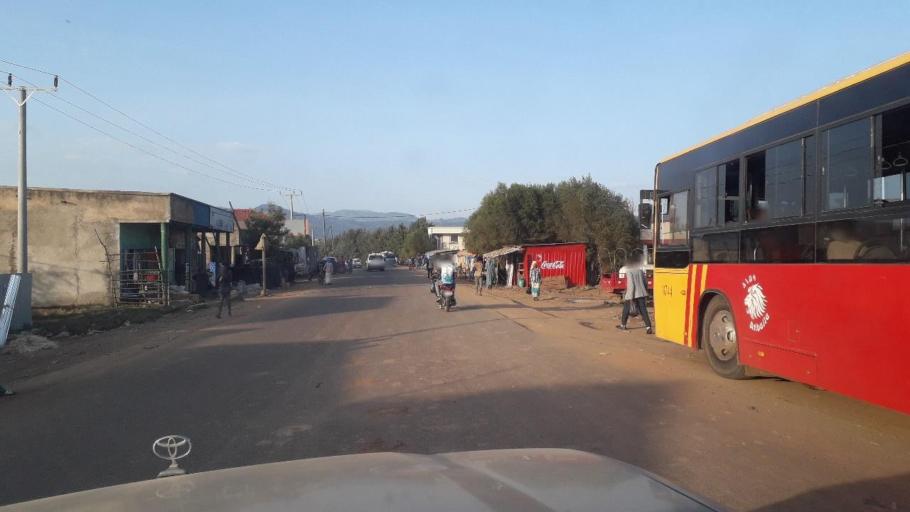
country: ET
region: Oromiya
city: Jima
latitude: 7.6447
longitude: 36.8436
